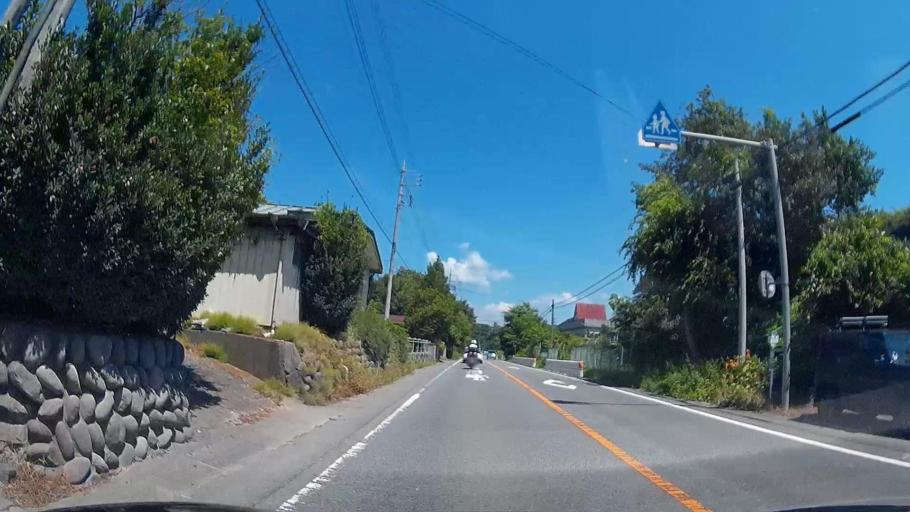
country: JP
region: Gunma
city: Numata
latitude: 36.5995
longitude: 139.0493
